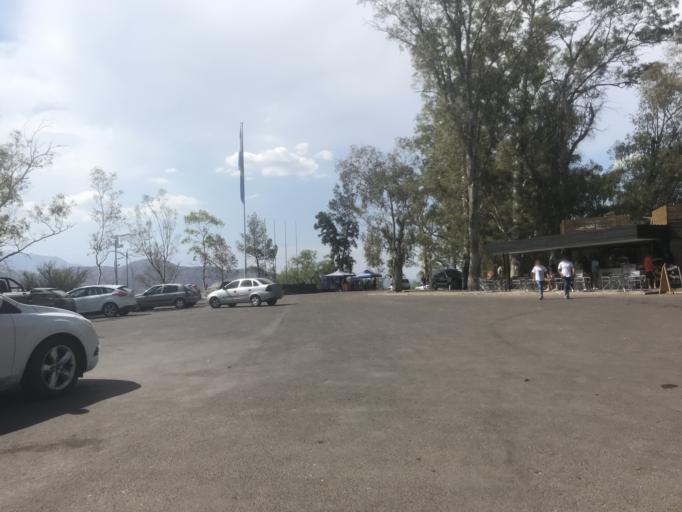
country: AR
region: Mendoza
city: Mendoza
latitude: -32.8881
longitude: -68.8911
